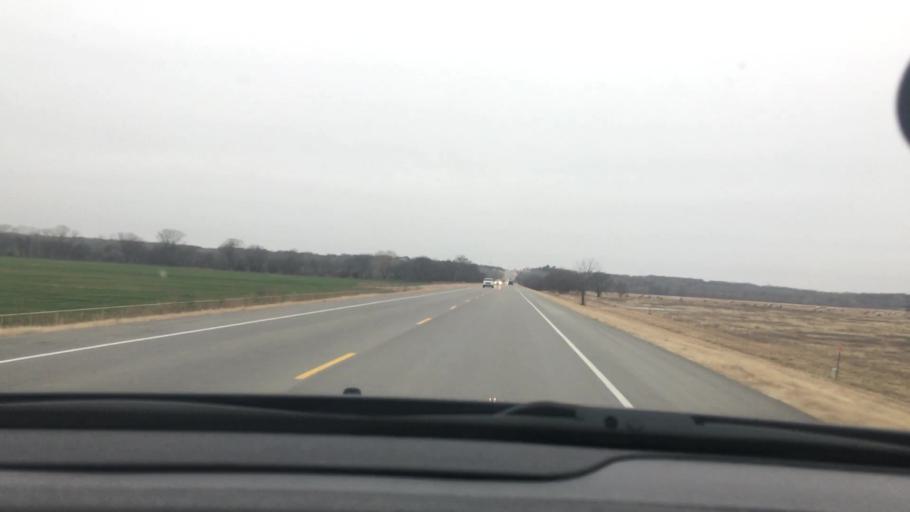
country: US
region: Oklahoma
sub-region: Garvin County
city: Wynnewood
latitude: 34.6227
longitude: -97.1861
